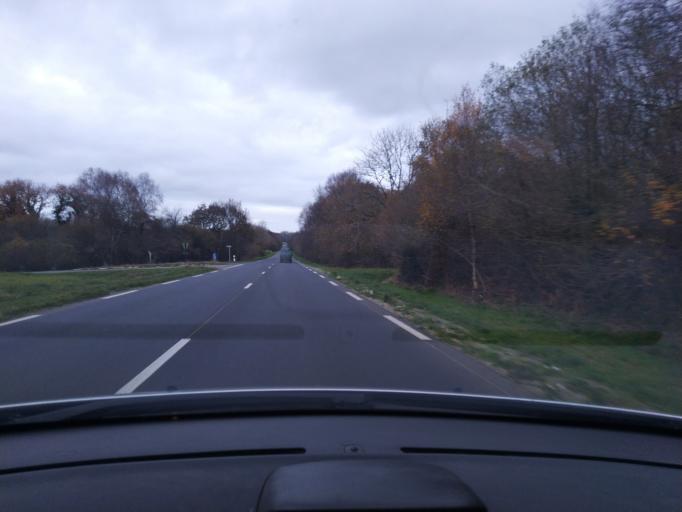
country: FR
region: Brittany
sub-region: Departement des Cotes-d'Armor
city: Plounevez-Moedec
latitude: 48.5713
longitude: -3.4951
